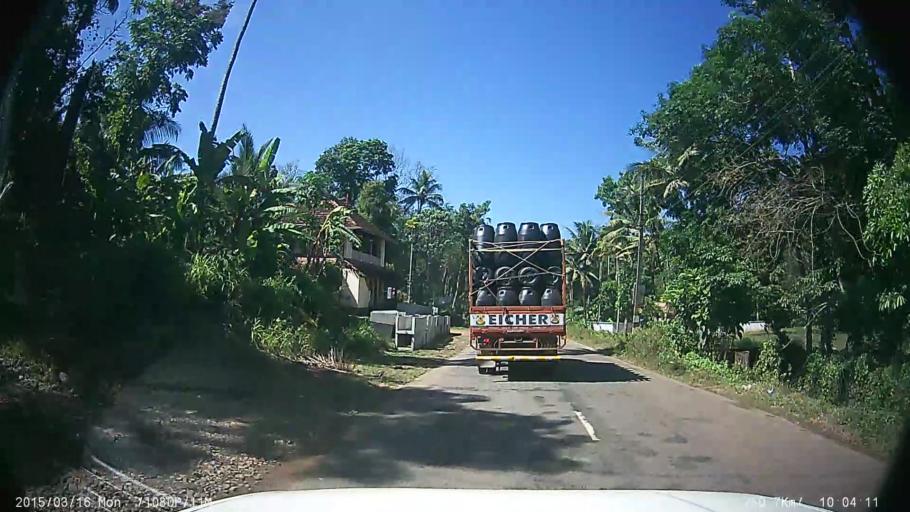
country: IN
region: Kerala
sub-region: Kottayam
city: Palackattumala
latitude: 9.7759
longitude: 76.5737
